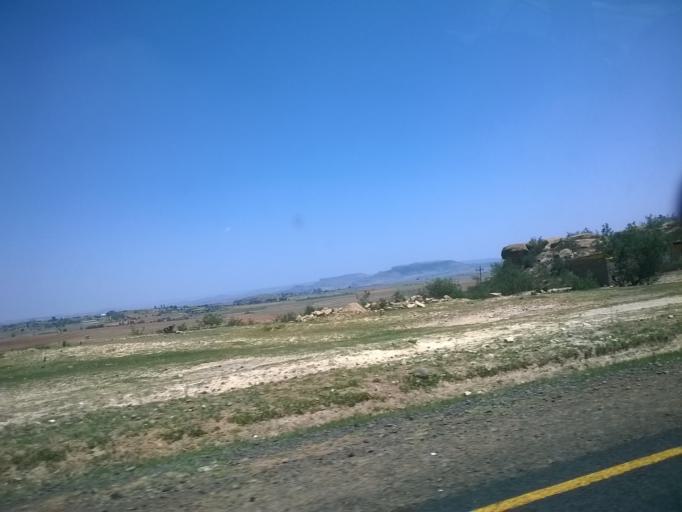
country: LS
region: Berea
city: Teyateyaneng
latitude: -29.1085
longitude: 27.8241
